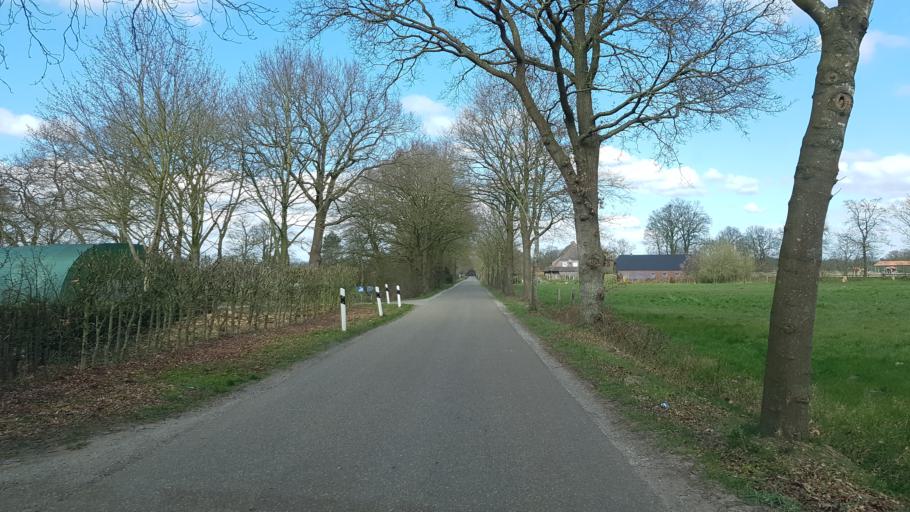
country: DE
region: Lower Saxony
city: Edewecht
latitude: 53.1638
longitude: 7.9372
